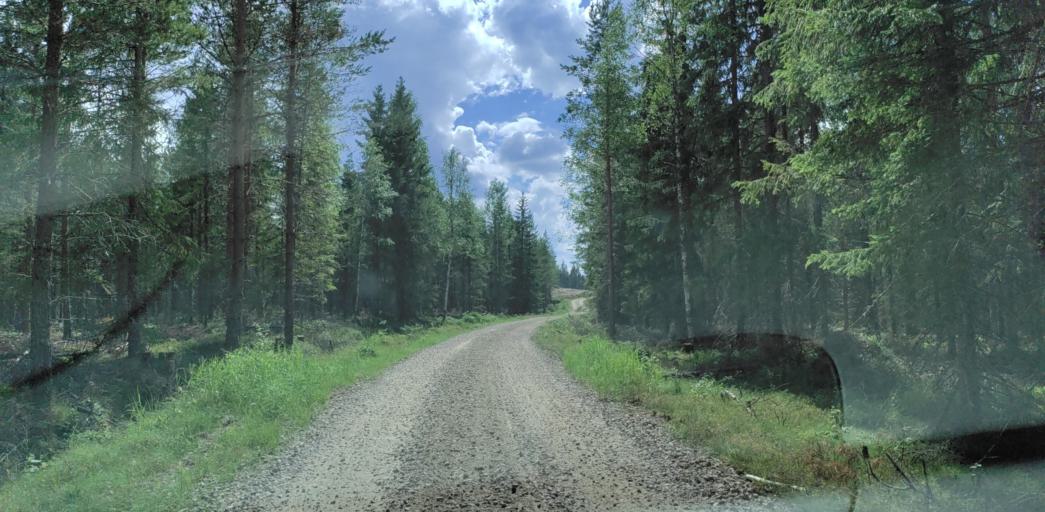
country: SE
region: Vaermland
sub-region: Hagfors Kommun
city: Ekshaerad
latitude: 60.0714
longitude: 13.3457
